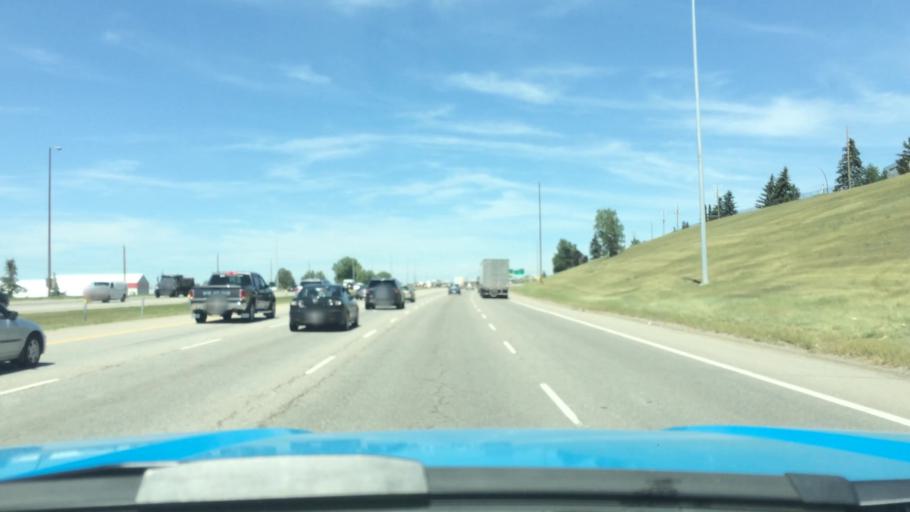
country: CA
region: Alberta
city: Calgary
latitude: 51.0877
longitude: -114.0384
